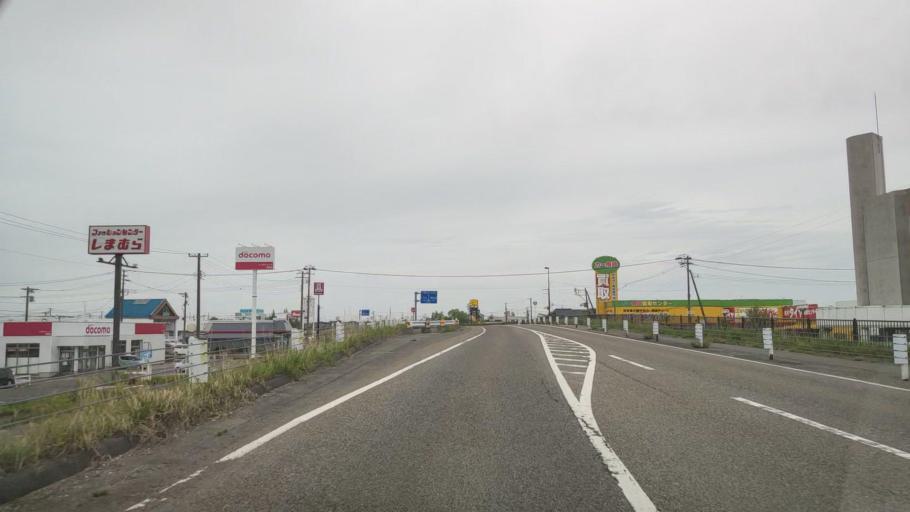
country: JP
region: Niigata
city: Niitsu-honcho
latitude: 37.7905
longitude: 139.1112
